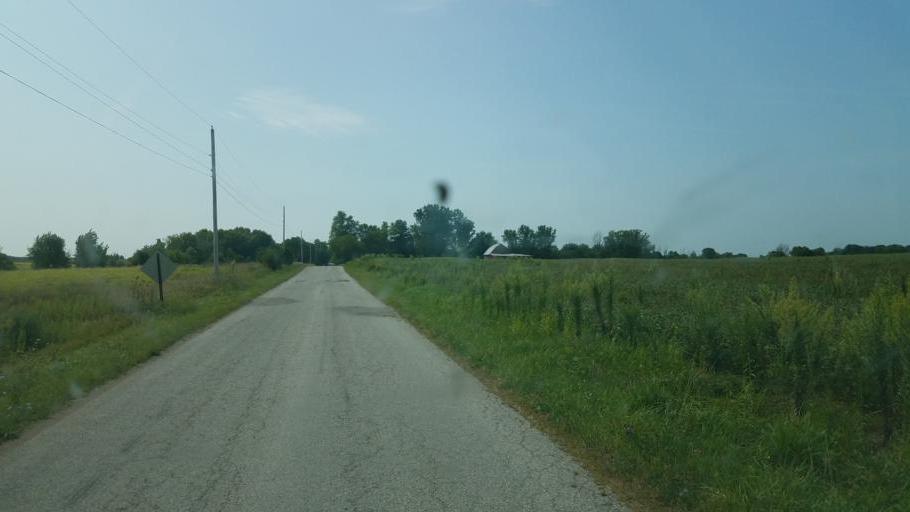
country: US
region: Ohio
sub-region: Delaware County
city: Ashley
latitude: 40.4425
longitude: -83.0102
